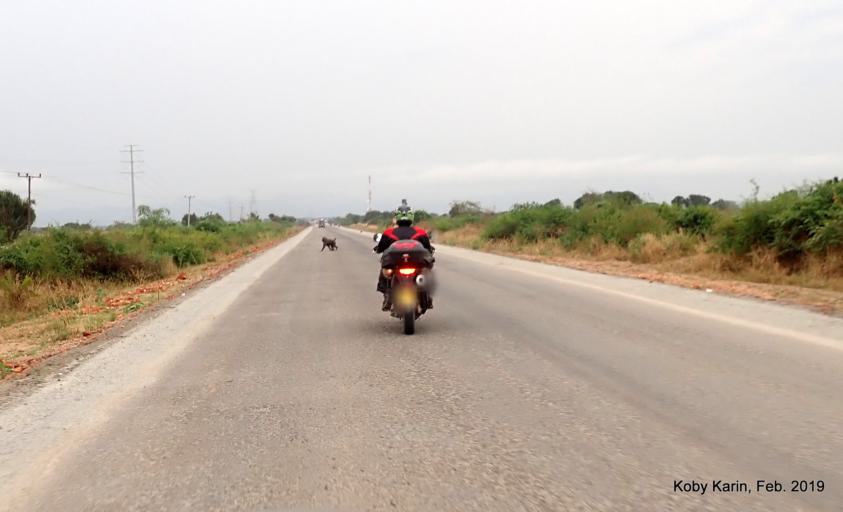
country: UG
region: Western Region
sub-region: Rubirizi District
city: Rubirizi
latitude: -0.1086
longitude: 30.0427
